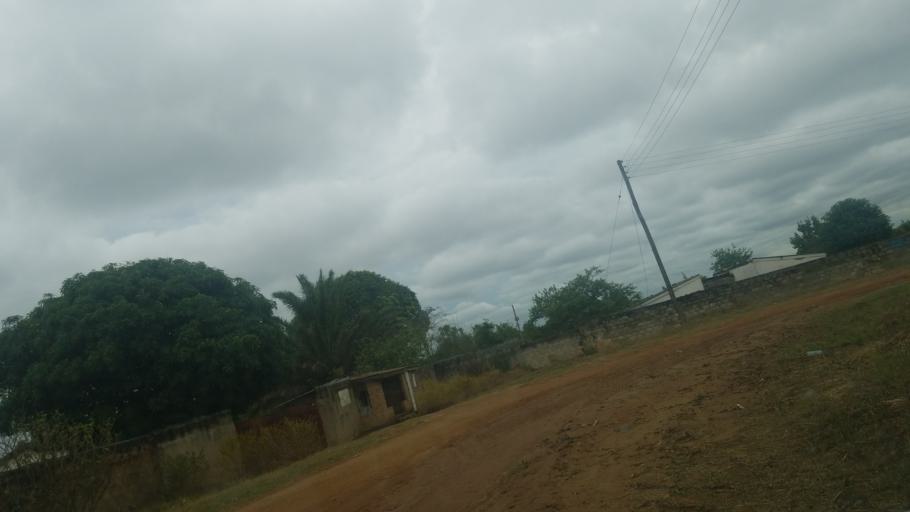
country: ZM
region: Luapula
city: Mansa
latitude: -11.1957
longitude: 28.8980
